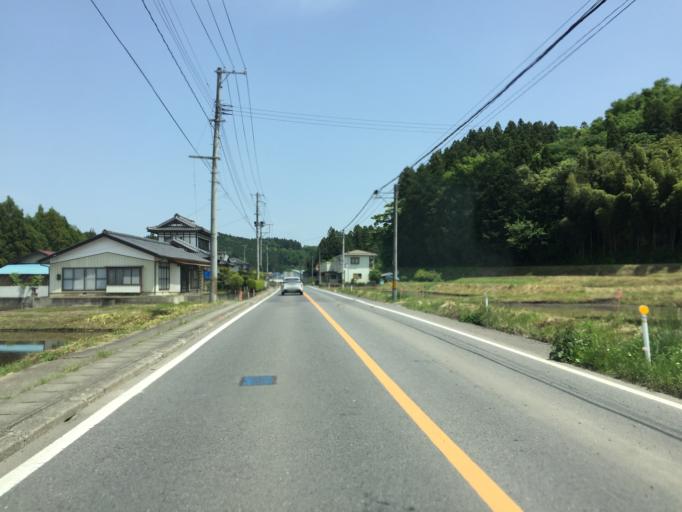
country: JP
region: Fukushima
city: Ishikawa
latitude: 37.1419
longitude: 140.4117
